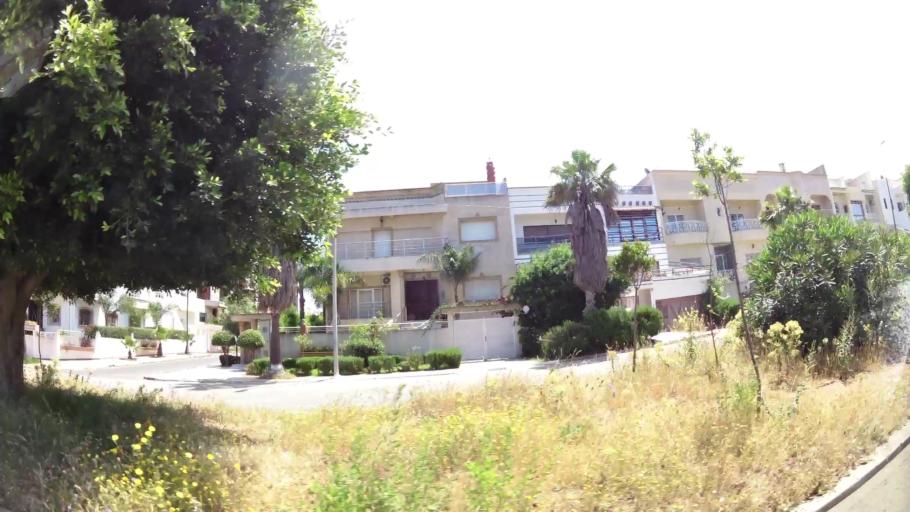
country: MA
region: Gharb-Chrarda-Beni Hssen
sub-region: Kenitra Province
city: Kenitra
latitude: 34.2739
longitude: -6.6136
